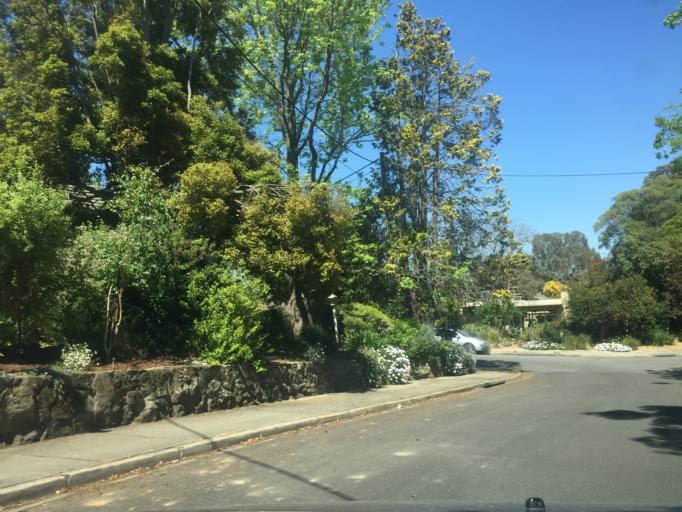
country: AU
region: Victoria
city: Ivanhoe East
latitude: -37.7701
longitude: 145.0589
